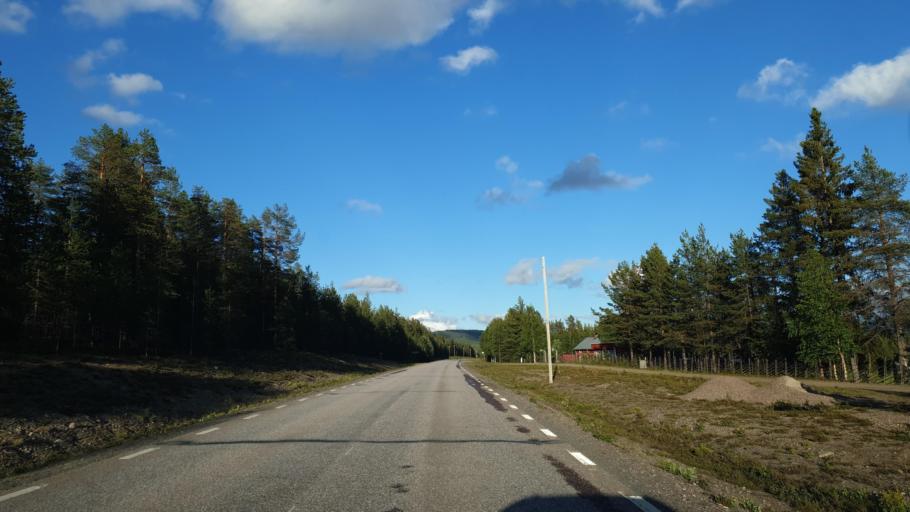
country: SE
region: Norrbotten
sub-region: Arvidsjaurs Kommun
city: Arvidsjaur
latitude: 65.7294
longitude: 18.6573
